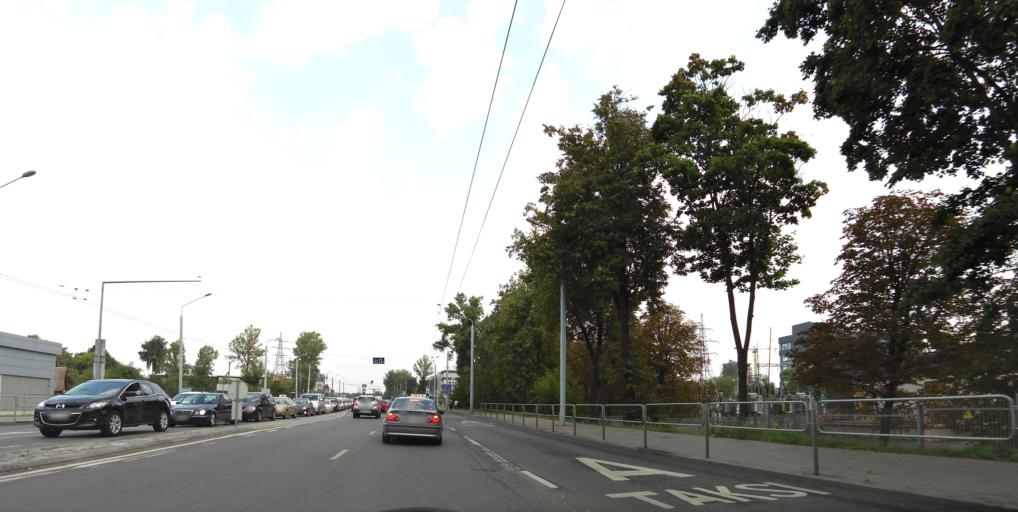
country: LT
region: Vilnius County
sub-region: Vilnius
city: Vilnius
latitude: 54.7136
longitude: 25.2869
